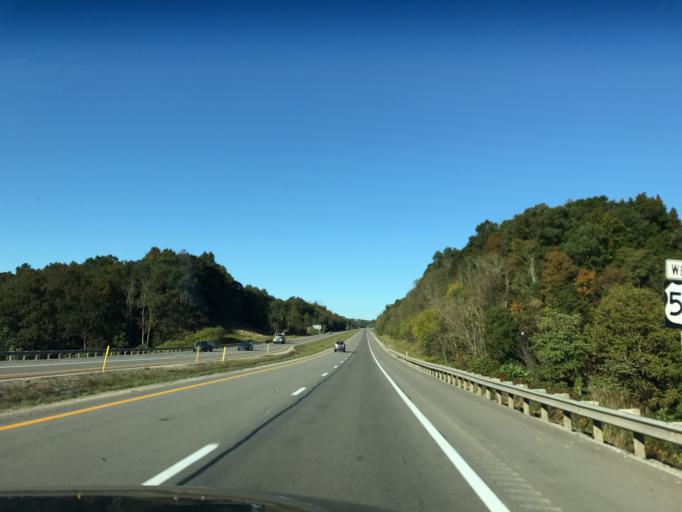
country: US
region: West Virginia
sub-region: Wood County
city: Mineral Wells
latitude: 39.2415
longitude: -81.4253
